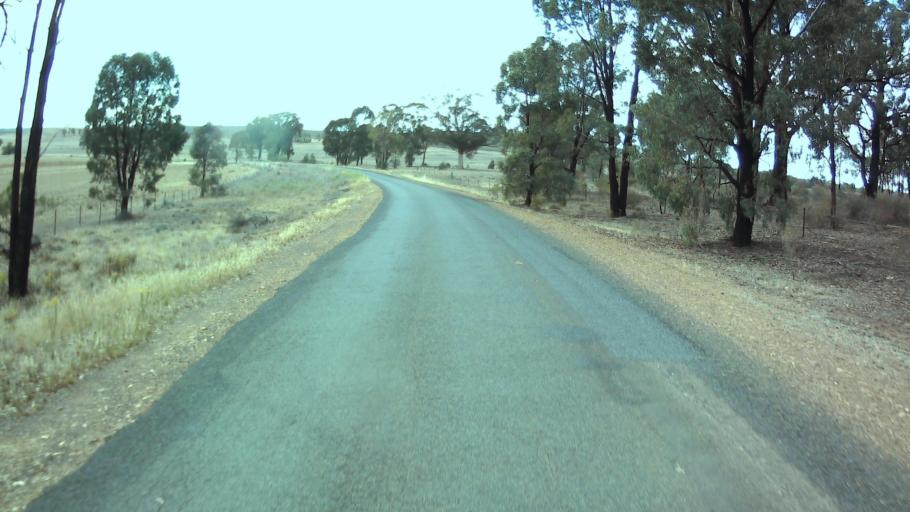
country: AU
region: New South Wales
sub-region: Weddin
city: Grenfell
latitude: -33.8446
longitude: 148.2425
